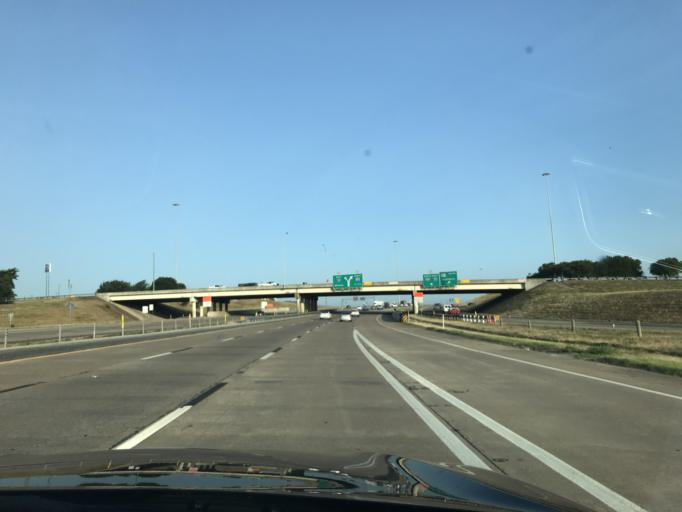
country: US
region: Texas
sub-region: Tarrant County
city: Benbrook
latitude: 32.6842
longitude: -97.4575
